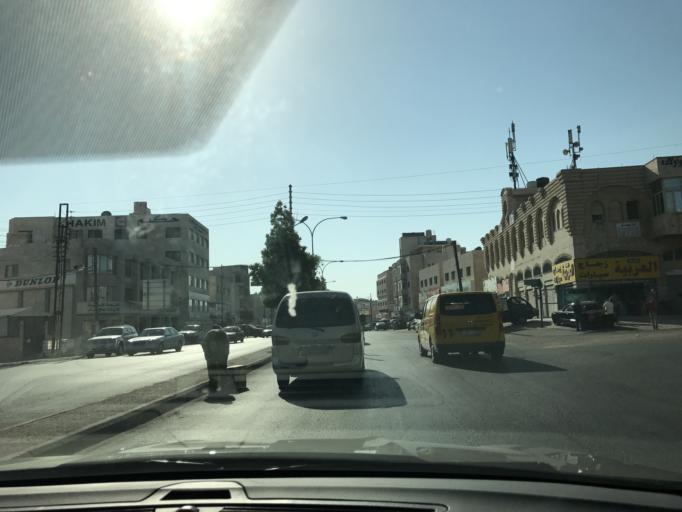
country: JO
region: Amman
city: Wadi as Sir
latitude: 31.9456
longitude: 35.8477
